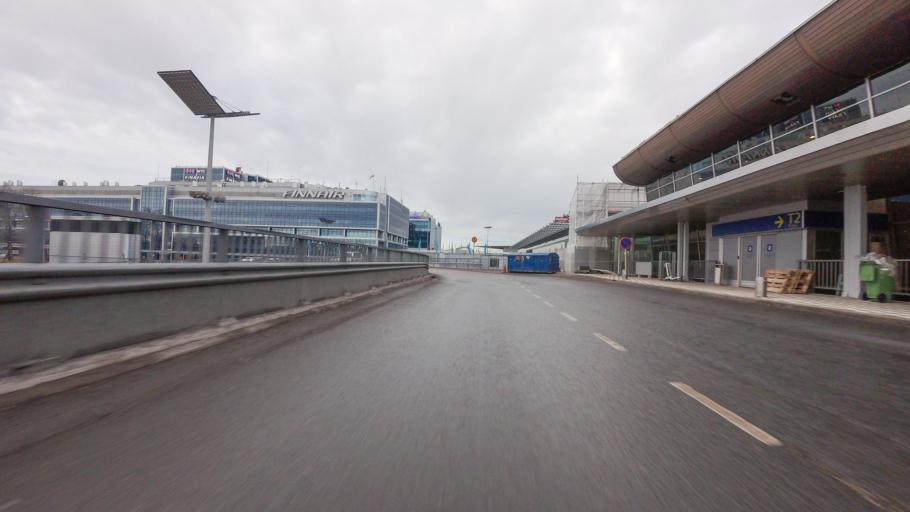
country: FI
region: Uusimaa
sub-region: Helsinki
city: Vantaa
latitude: 60.3179
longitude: 24.9662
